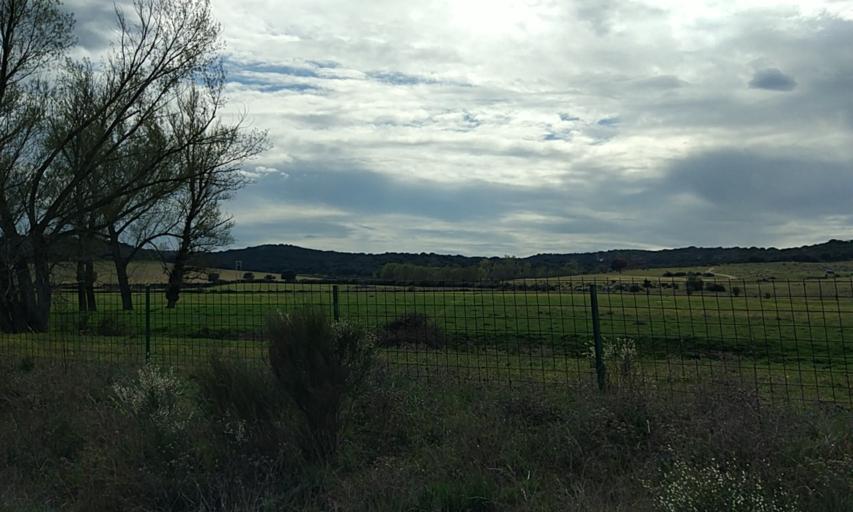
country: ES
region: Castille and Leon
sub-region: Provincia de Salamanca
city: Pastores
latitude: 40.5186
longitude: -6.5675
